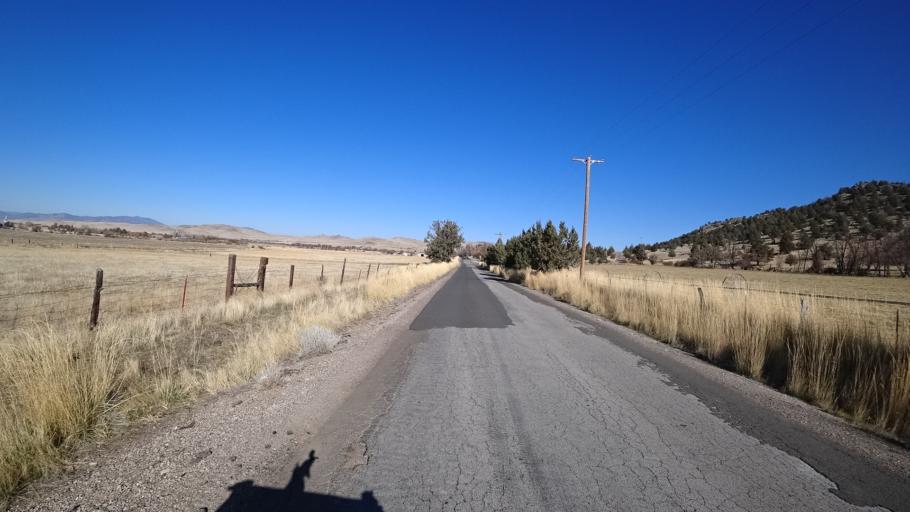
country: US
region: California
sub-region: Siskiyou County
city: Montague
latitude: 41.7070
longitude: -122.3793
